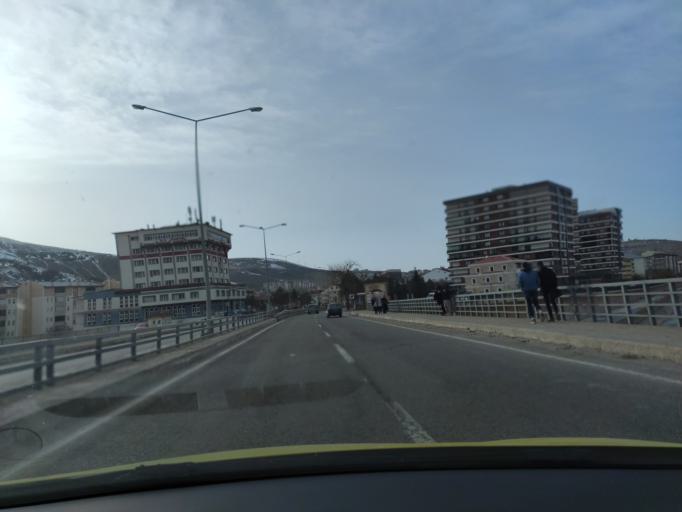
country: TR
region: Bayburt
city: Bayburt
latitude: 40.2445
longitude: 40.2368
